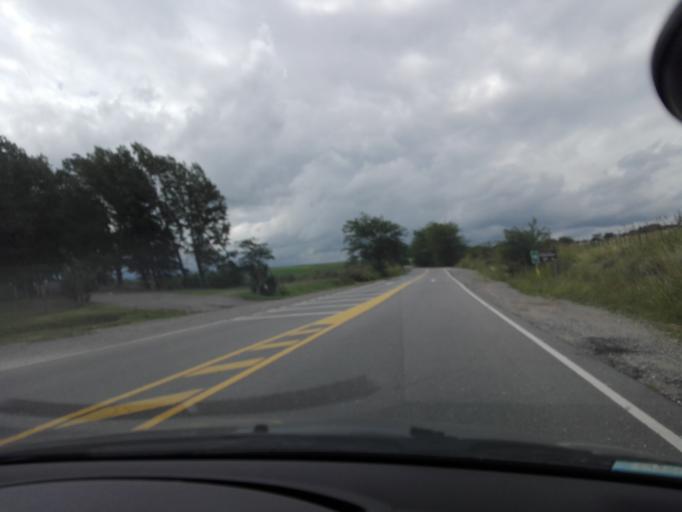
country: AR
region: Cordoba
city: Cuesta Blanca
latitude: -31.6063
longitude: -64.5611
